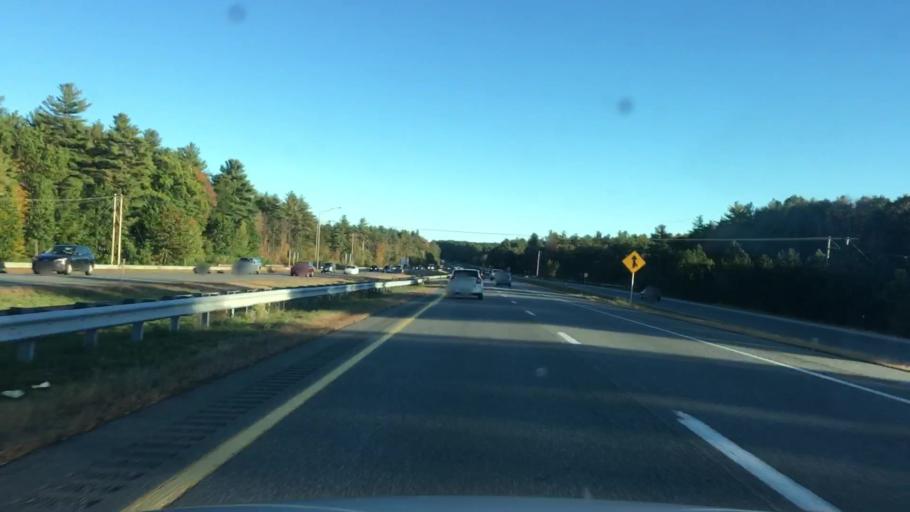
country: US
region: New Hampshire
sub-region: Rockingham County
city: Exeter
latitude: 42.9903
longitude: -70.9246
